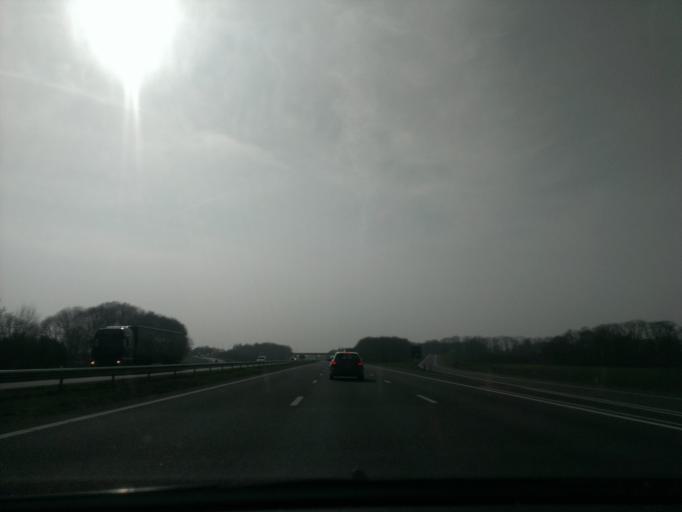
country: NL
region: Gelderland
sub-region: Gemeente Lochem
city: Laren
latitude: 52.2504
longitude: 6.4061
